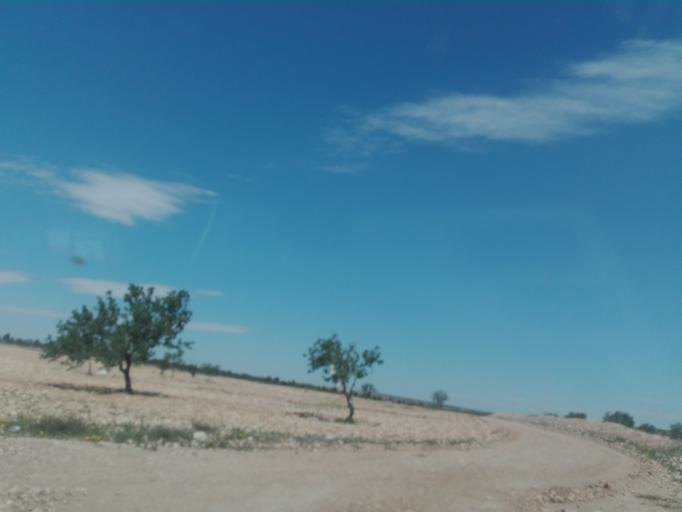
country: TN
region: Safaqis
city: Sfax
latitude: 34.6892
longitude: 10.5309
